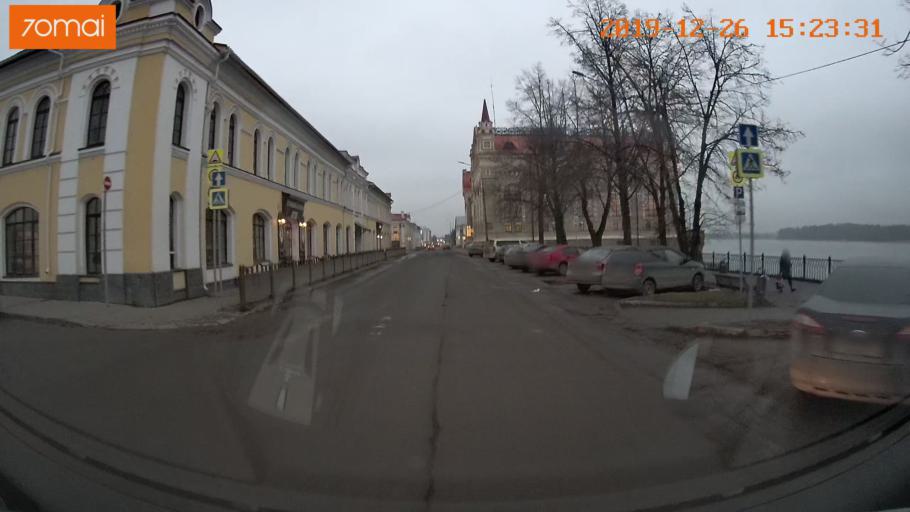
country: RU
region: Jaroslavl
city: Rybinsk
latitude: 58.0490
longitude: 38.8578
